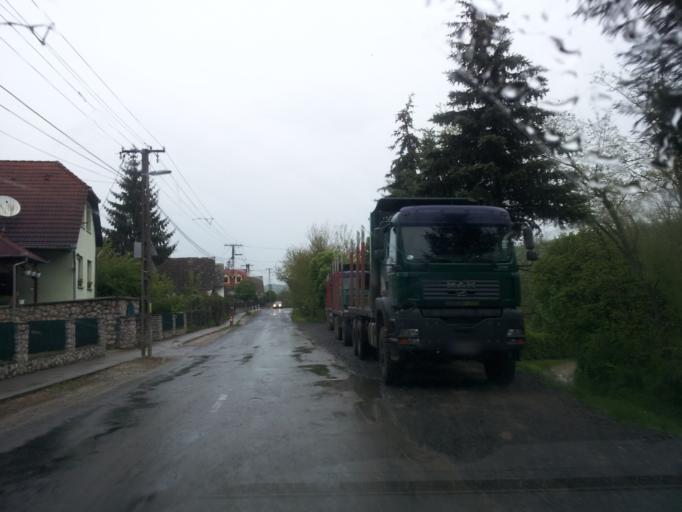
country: HU
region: Tolna
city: Szentgalpuszta
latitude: 46.2749
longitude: 18.6389
